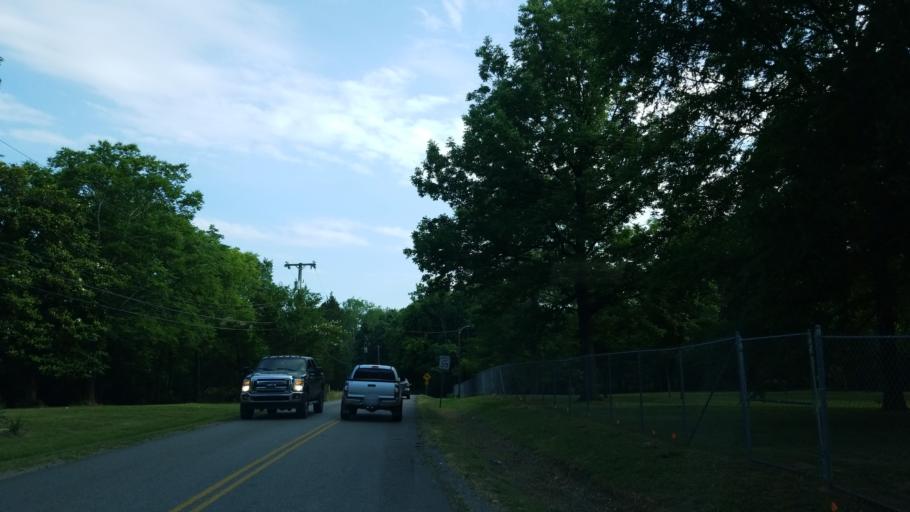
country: US
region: Tennessee
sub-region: Rutherford County
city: La Vergne
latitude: 36.0407
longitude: -86.5957
